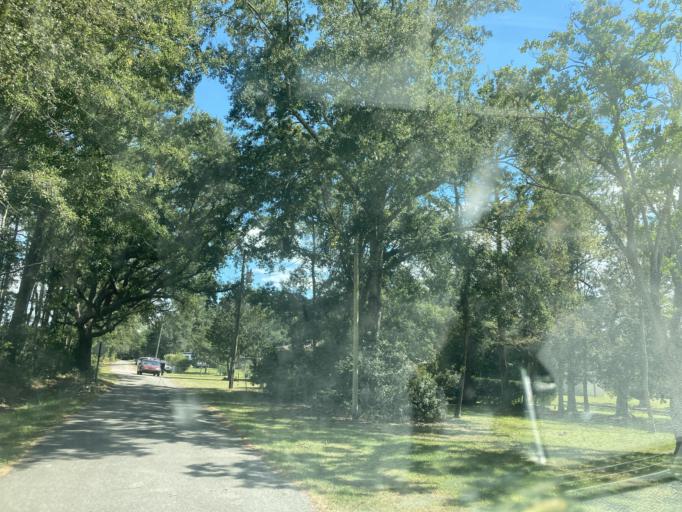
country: US
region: Mississippi
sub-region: Jackson County
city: Gulf Hills
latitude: 30.4485
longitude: -88.8450
